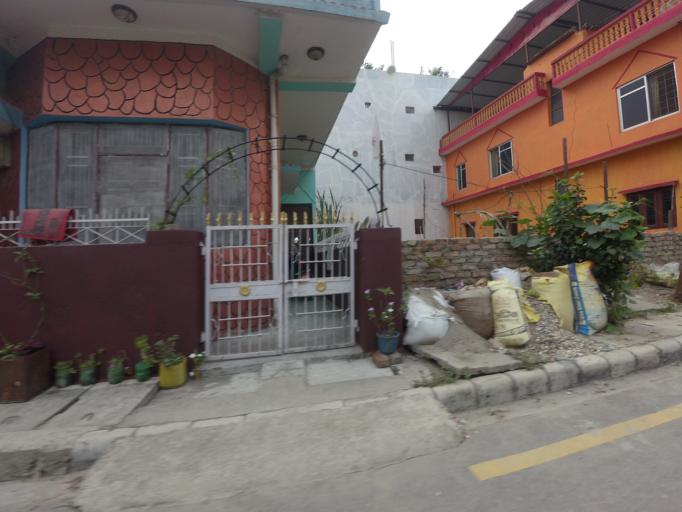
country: NP
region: Western Region
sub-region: Lumbini Zone
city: Bhairahawa
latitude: 27.5197
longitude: 83.4451
